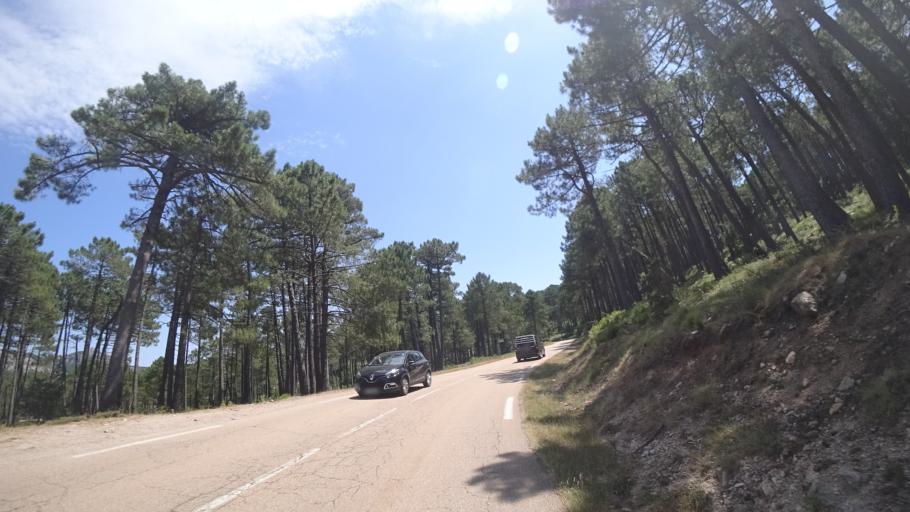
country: FR
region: Corsica
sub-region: Departement de la Corse-du-Sud
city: Zonza
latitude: 41.6854
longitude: 9.1976
